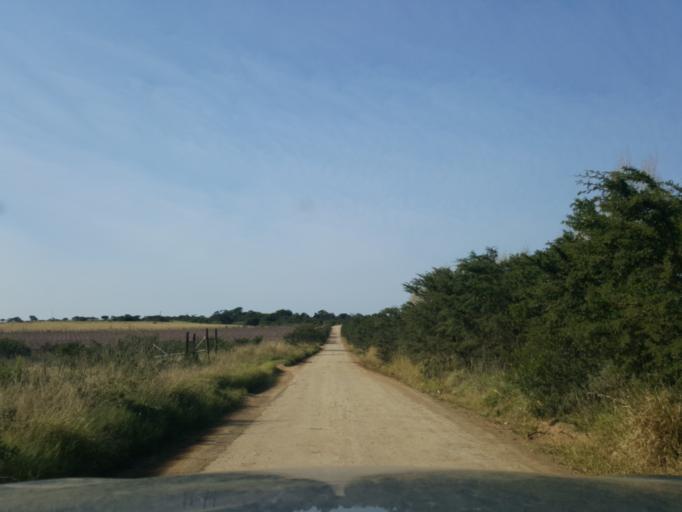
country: ZA
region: Eastern Cape
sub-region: Cacadu District Municipality
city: Grahamstown
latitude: -33.4143
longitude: 26.3131
